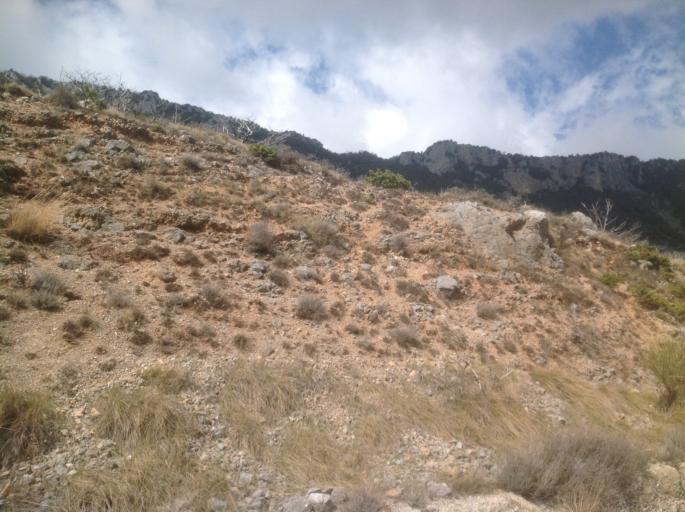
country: IT
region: Calabria
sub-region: Provincia di Cosenza
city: Civita
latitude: 39.8383
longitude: 16.3050
